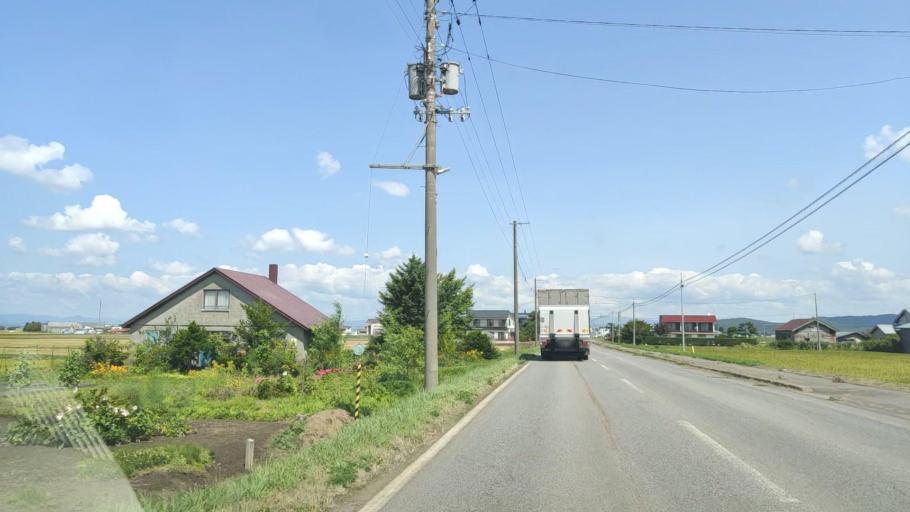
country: JP
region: Hokkaido
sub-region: Asahikawa-shi
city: Asahikawa
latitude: 43.7216
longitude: 142.4579
